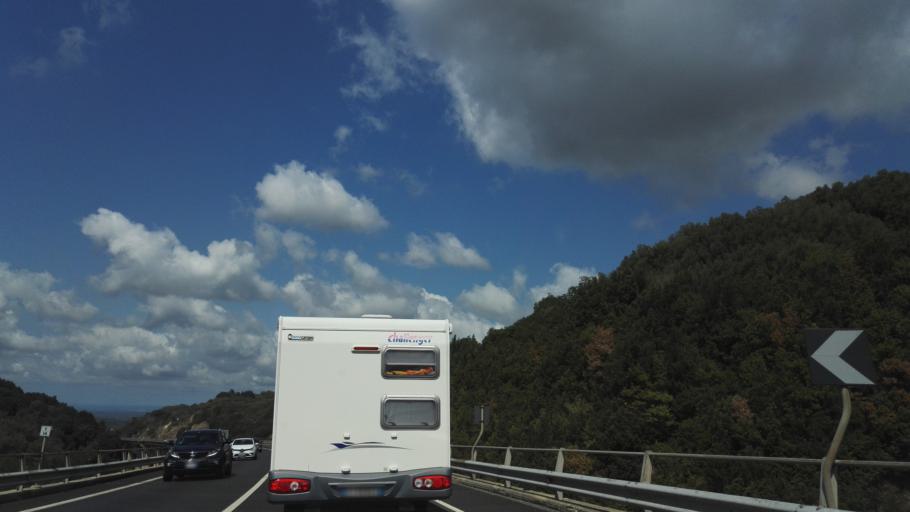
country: IT
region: Calabria
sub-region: Provincia di Reggio Calabria
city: Anoia Superiore
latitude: 38.4168
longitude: 16.1250
